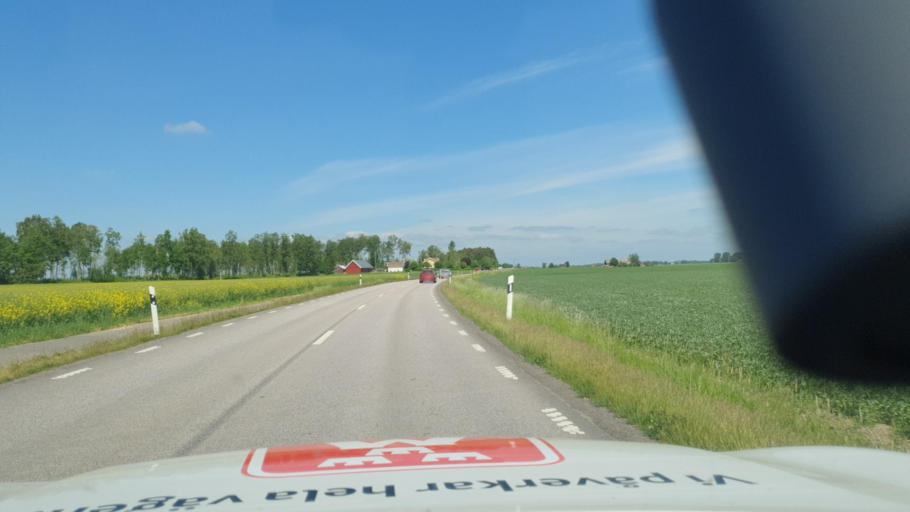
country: SE
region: Vaestra Goetaland
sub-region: Vara Kommun
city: Vara
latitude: 58.2773
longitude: 12.9549
